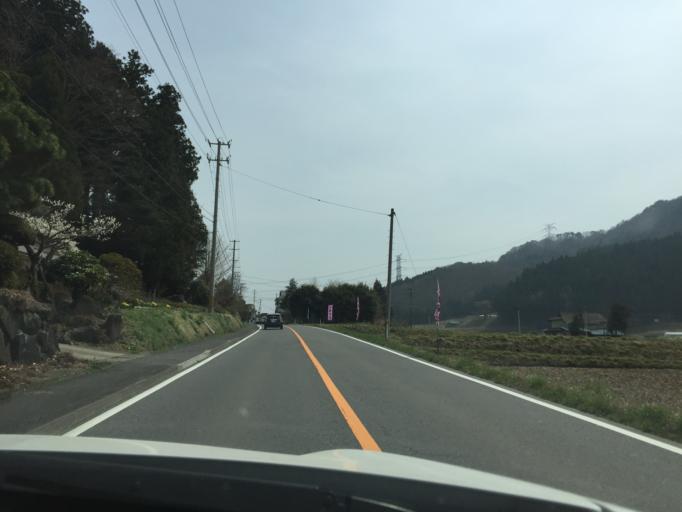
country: JP
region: Fukushima
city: Ishikawa
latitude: 37.1284
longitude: 140.4968
